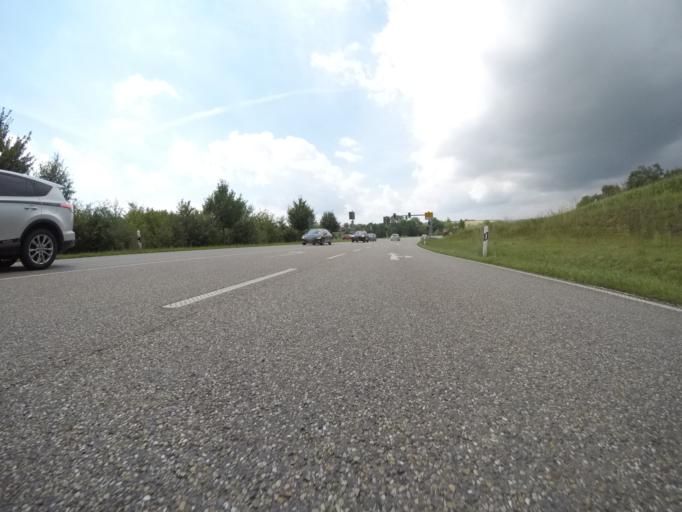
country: DE
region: Baden-Wuerttemberg
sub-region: Regierungsbezirk Stuttgart
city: Schwieberdingen
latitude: 48.8624
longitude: 9.0948
